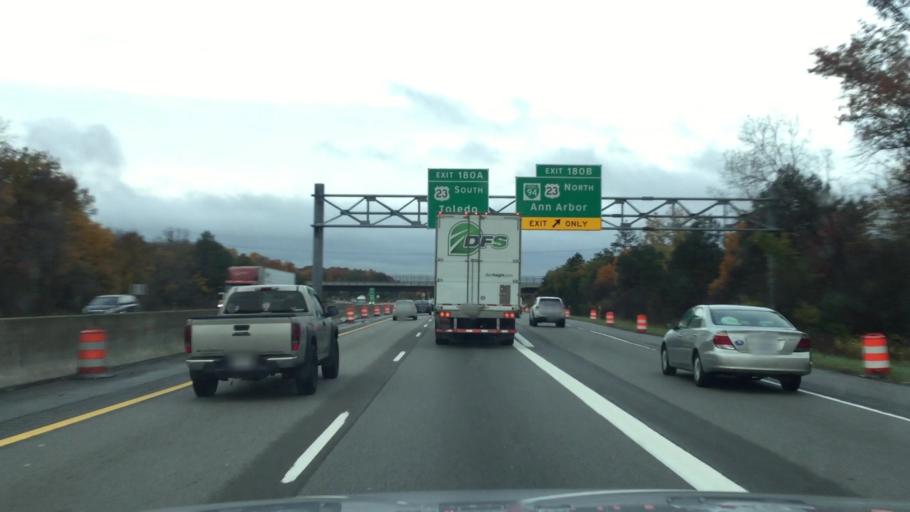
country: US
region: Michigan
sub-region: Washtenaw County
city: Ypsilanti
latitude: 42.2248
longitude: -83.6765
